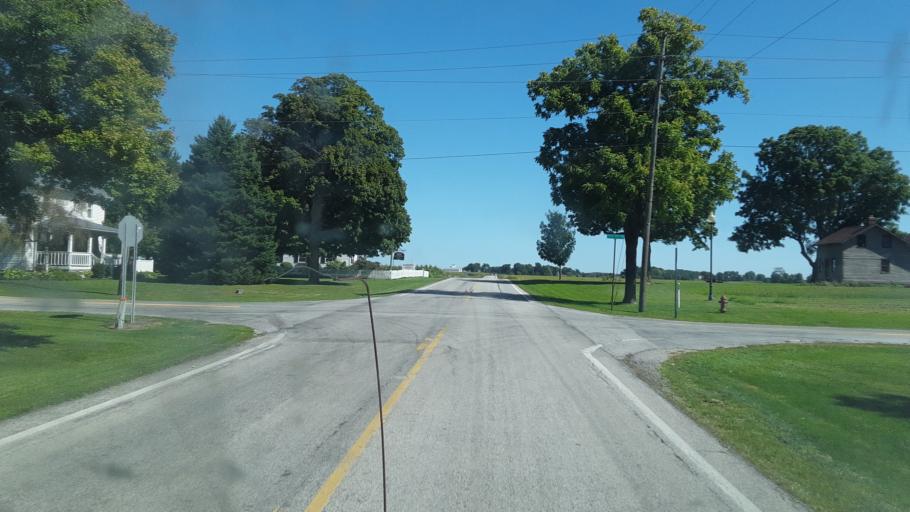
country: US
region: Ohio
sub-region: Huron County
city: Monroeville
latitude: 41.2271
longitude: -82.7579
